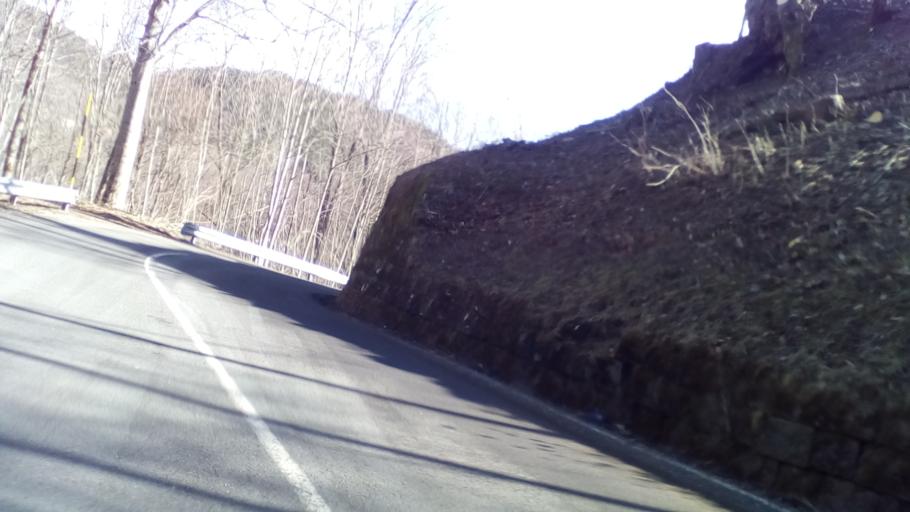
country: IT
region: Emilia-Romagna
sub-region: Provincia di Modena
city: Pievepelago
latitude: 44.1898
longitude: 10.5590
